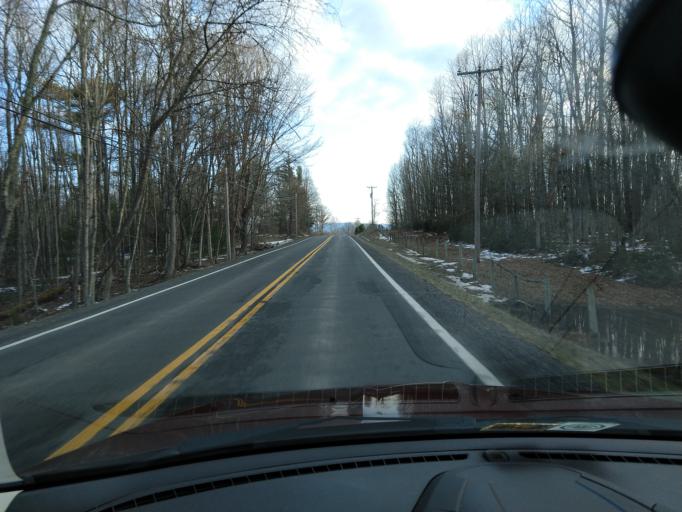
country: US
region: West Virginia
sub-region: Pocahontas County
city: Marlinton
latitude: 38.0864
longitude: -80.2792
